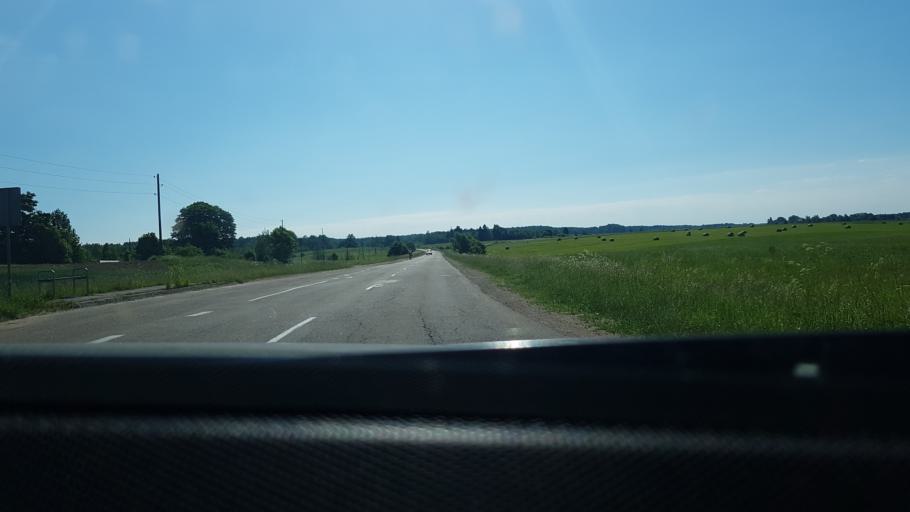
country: LV
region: Daugavpils
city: Daugavpils
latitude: 55.8186
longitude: 26.8005
